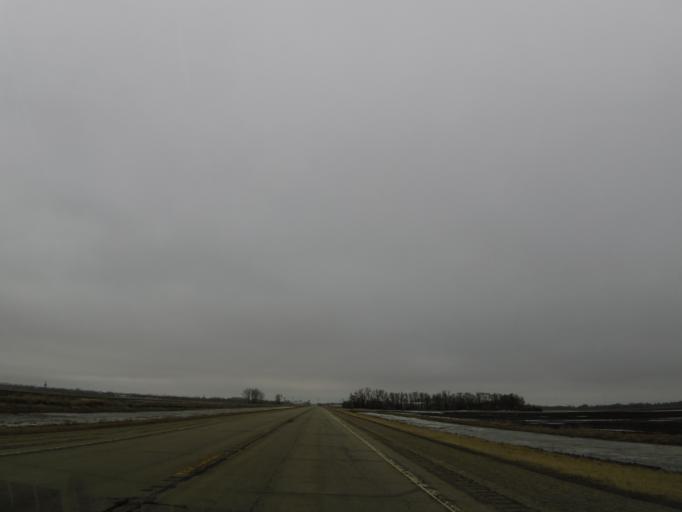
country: US
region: North Dakota
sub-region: Walsh County
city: Grafton
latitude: 48.4471
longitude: -97.4192
